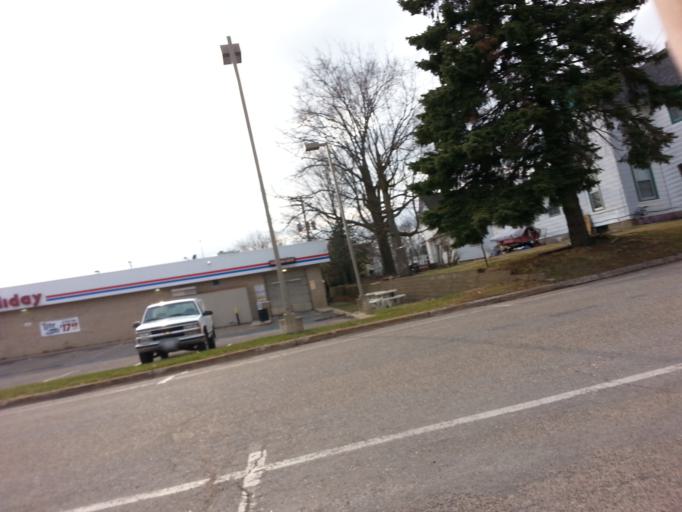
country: US
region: Wisconsin
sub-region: Pierce County
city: Ellsworth
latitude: 44.7326
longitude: -92.4858
